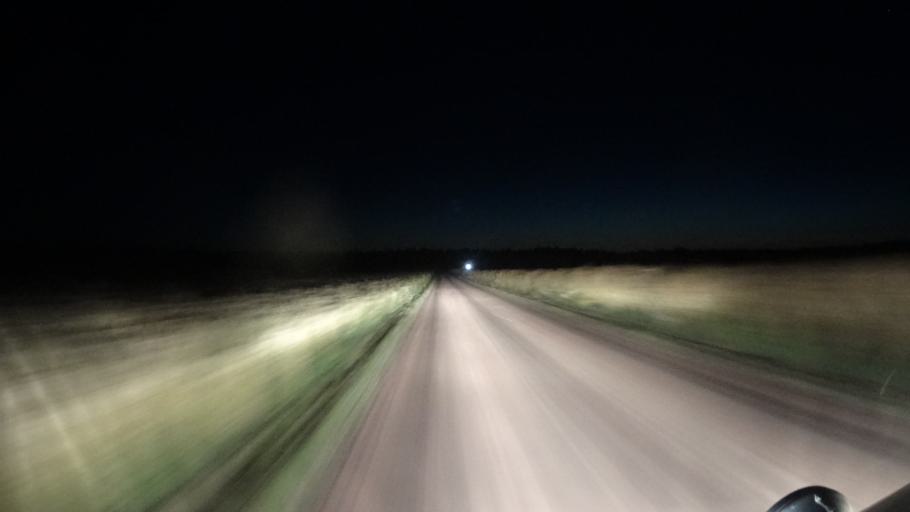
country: SE
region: OEstergoetland
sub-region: Vadstena Kommun
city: Herrestad
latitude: 58.3269
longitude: 14.8249
